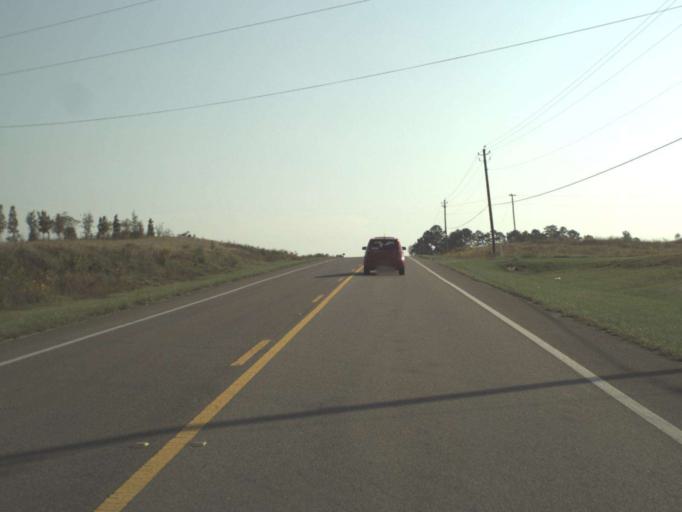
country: US
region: Florida
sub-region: Holmes County
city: Bonifay
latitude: 30.5925
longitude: -85.7849
